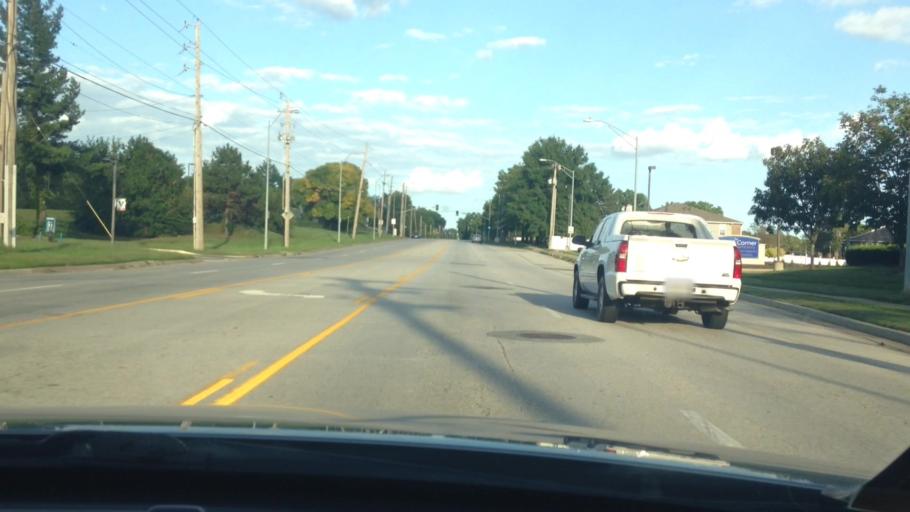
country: US
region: Missouri
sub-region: Jackson County
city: Raytown
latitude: 38.9671
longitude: -94.5134
